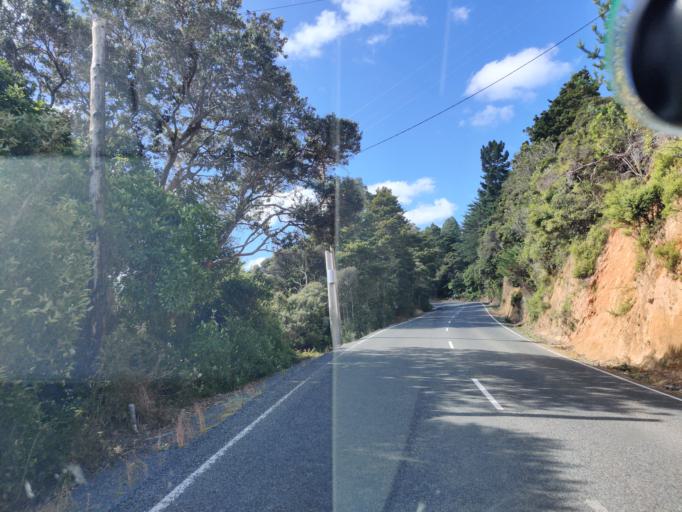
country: NZ
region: Northland
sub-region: Whangarei
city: Ngunguru
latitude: -35.6087
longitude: 174.5235
